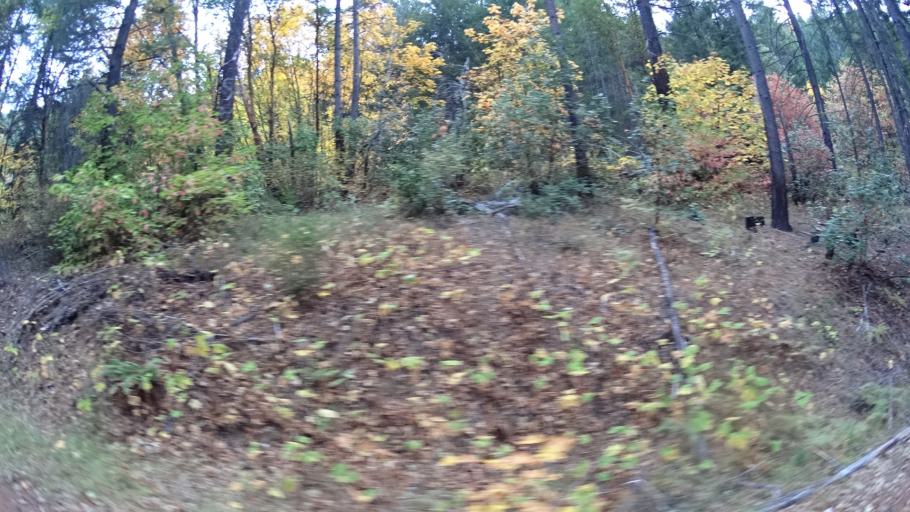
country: US
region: California
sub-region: Siskiyou County
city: Happy Camp
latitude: 41.8276
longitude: -123.3286
